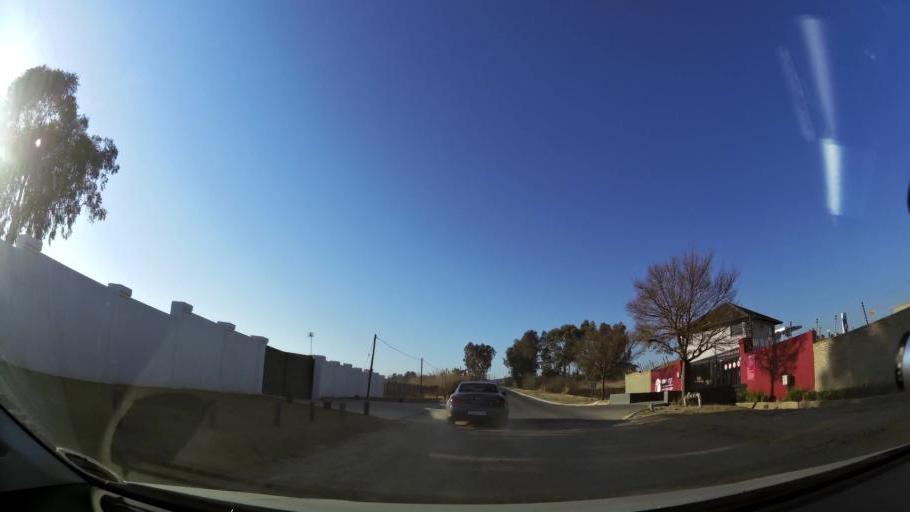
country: ZA
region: Gauteng
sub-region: City of Johannesburg Metropolitan Municipality
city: Midrand
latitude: -26.0297
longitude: 28.1365
